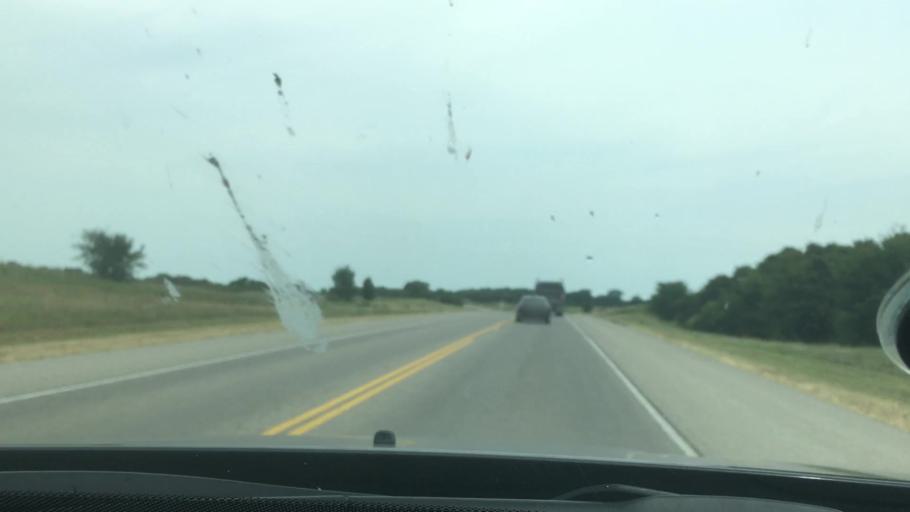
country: US
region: Oklahoma
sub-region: Pontotoc County
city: Ada
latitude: 34.6686
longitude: -96.5677
